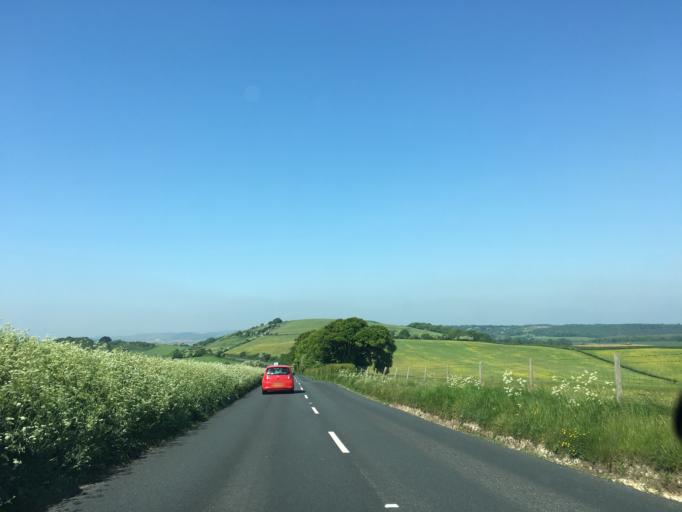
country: GB
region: England
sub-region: Isle of Wight
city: Newchurch
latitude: 50.6844
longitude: -1.1949
